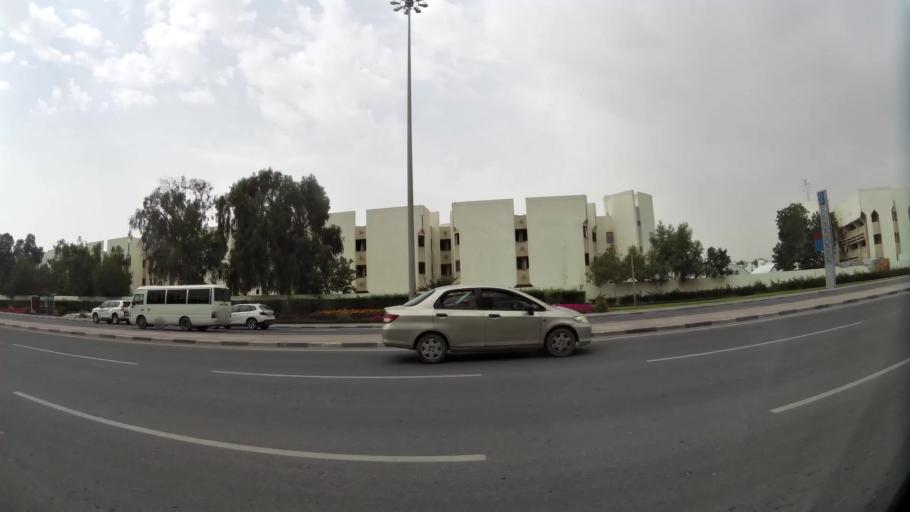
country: QA
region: Baladiyat ad Dawhah
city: Doha
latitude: 25.2982
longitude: 51.5035
